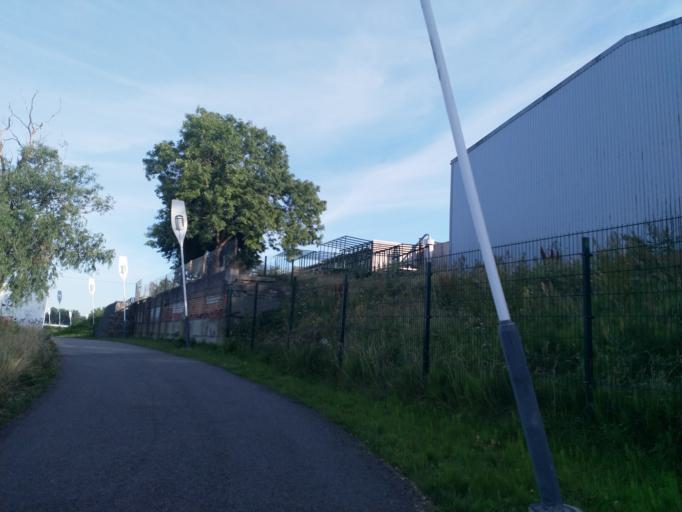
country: EE
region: Paernumaa
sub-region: Paernu linn
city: Parnu
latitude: 58.3841
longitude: 24.5296
